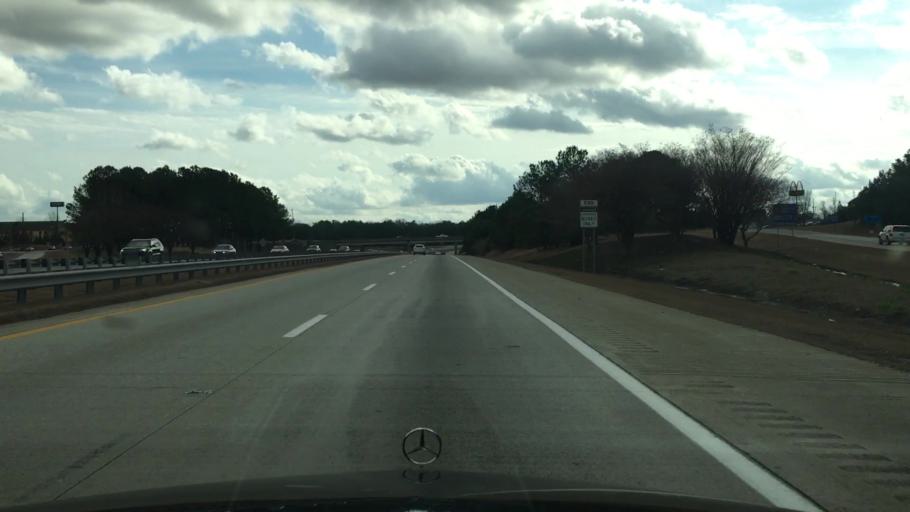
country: US
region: North Carolina
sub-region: Wake County
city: Garner
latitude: 35.6101
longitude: -78.5657
